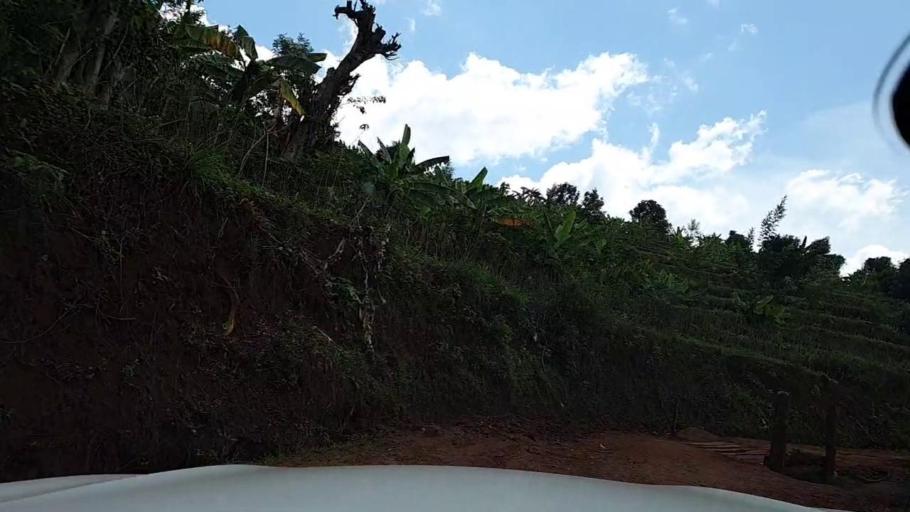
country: RW
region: Southern Province
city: Butare
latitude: -2.7510
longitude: 29.7623
